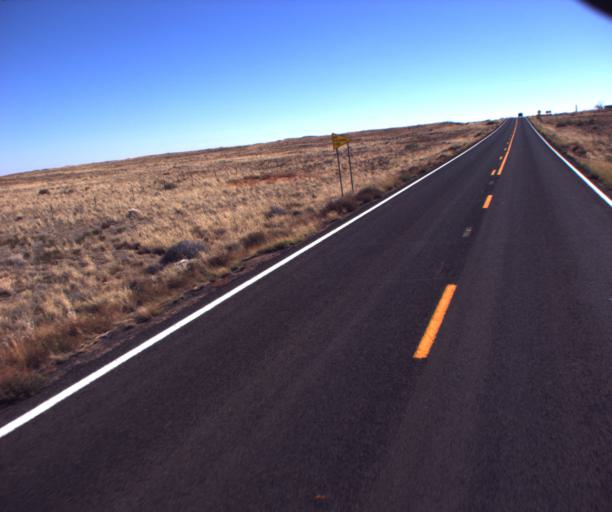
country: US
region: Arizona
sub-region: Coconino County
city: Tuba City
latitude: 35.9621
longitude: -110.9423
